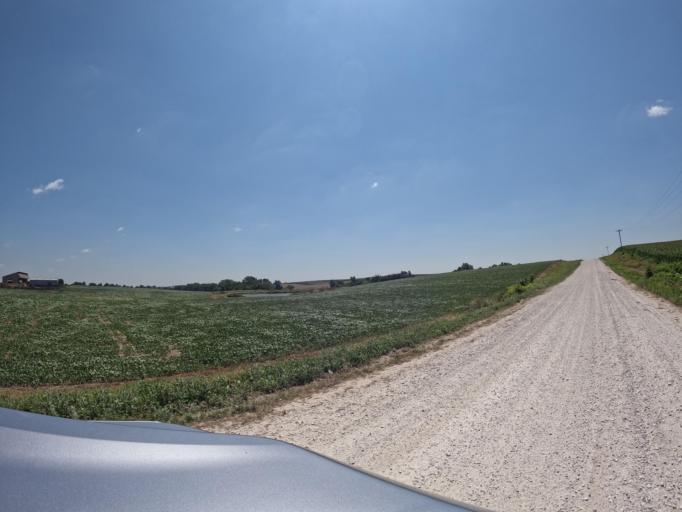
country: US
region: Iowa
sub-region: Keokuk County
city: Sigourney
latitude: 41.2786
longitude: -92.2381
